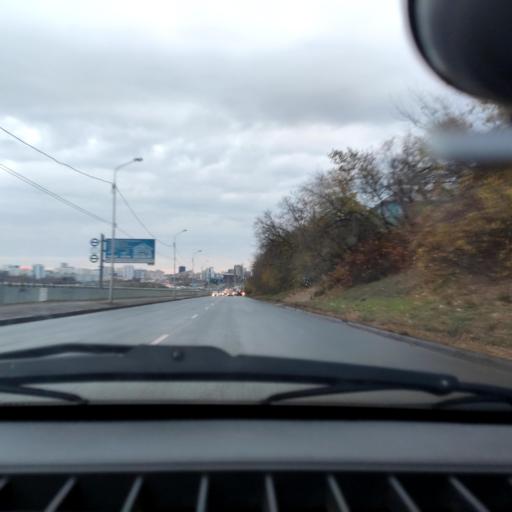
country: RU
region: Bashkortostan
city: Ufa
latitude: 54.7021
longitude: 55.9690
